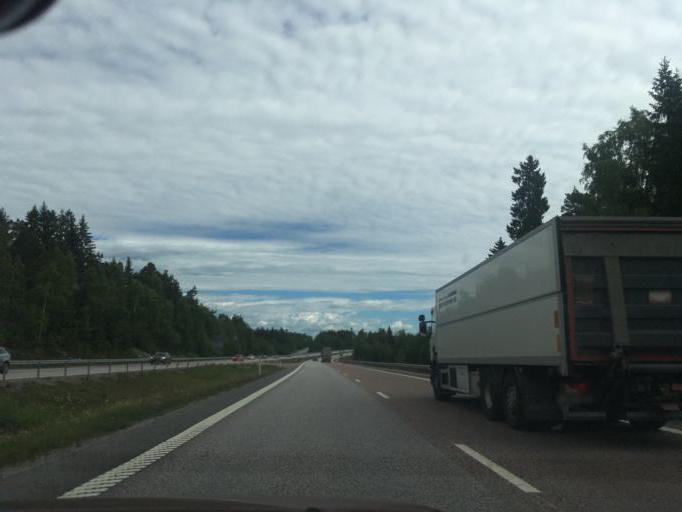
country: SE
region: Soedermanland
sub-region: Trosa Kommun
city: Vagnharad
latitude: 58.9257
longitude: 17.3937
